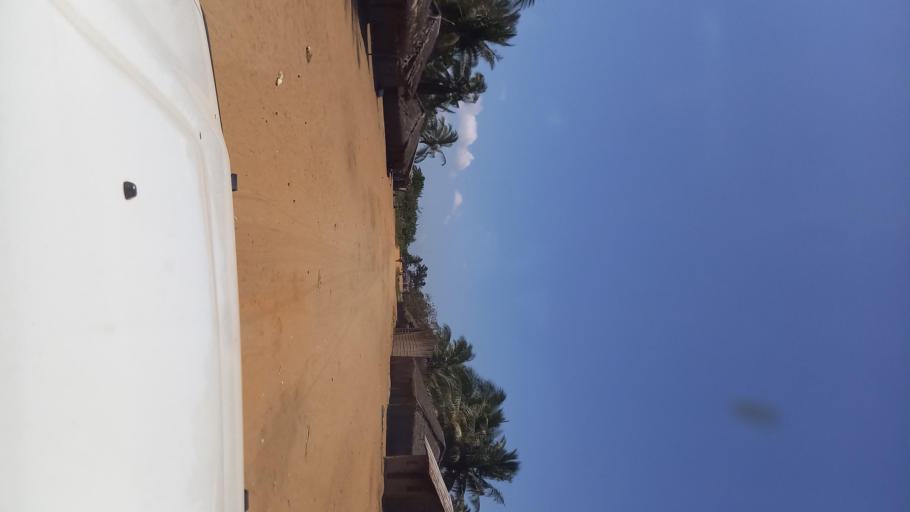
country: MZ
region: Cabo Delgado
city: Pemba
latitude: -13.4190
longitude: 40.5198
